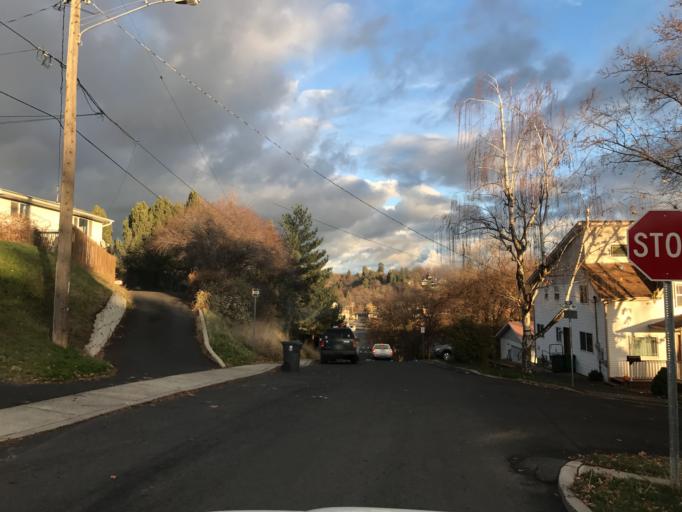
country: US
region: Idaho
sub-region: Latah County
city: Moscow
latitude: 46.7360
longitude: -117.0070
